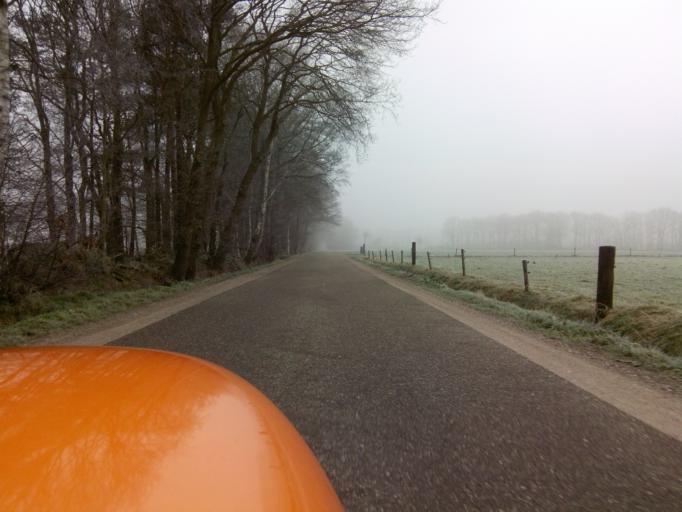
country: NL
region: Gelderland
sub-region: Gemeente Barneveld
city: Voorthuizen
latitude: 52.2003
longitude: 5.5848
